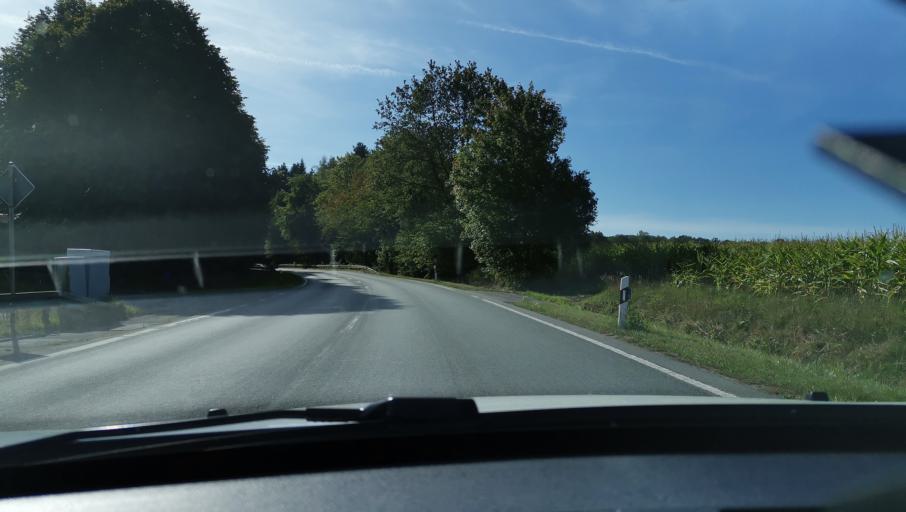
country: DE
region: North Rhine-Westphalia
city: Halver
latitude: 51.1994
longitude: 7.4880
